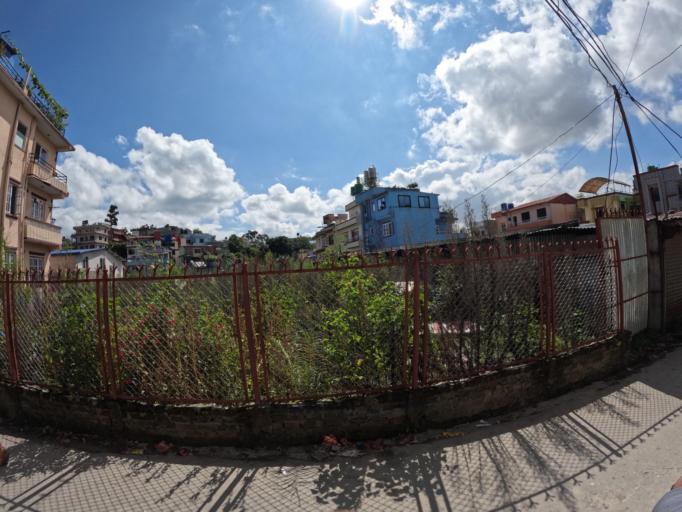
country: NP
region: Central Region
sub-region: Bagmati Zone
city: Kathmandu
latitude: 27.7479
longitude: 85.3320
